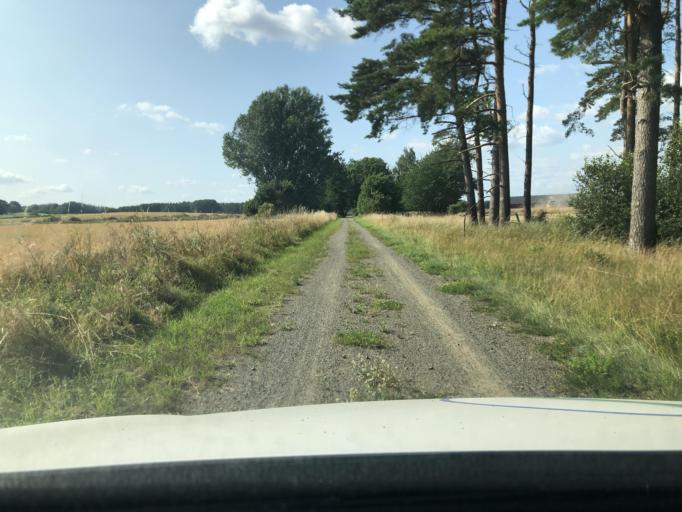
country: SE
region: Skane
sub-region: Kristianstads Kommun
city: Degeberga
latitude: 55.8157
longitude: 14.1272
